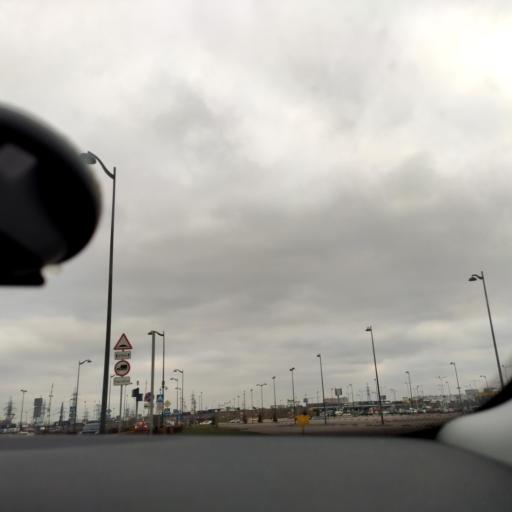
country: RU
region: Moskovskaya
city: Lyubertsy
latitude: 55.6584
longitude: 37.8806
